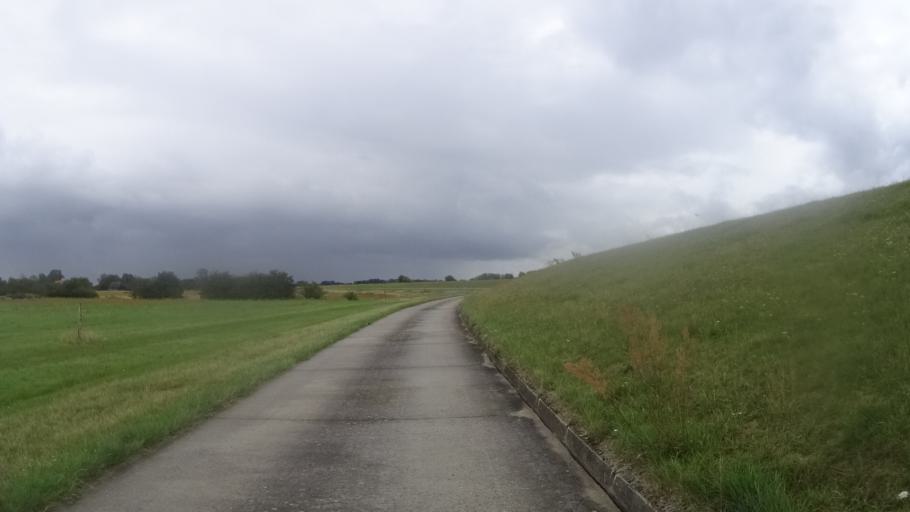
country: DE
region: Lower Saxony
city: Neu Darchau
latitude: 53.2578
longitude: 10.8496
